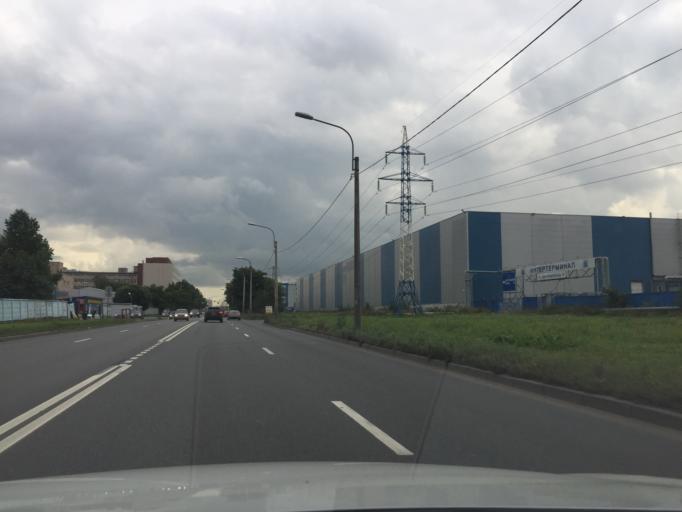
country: RU
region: St.-Petersburg
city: Dachnoye
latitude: 59.8444
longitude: 30.2946
